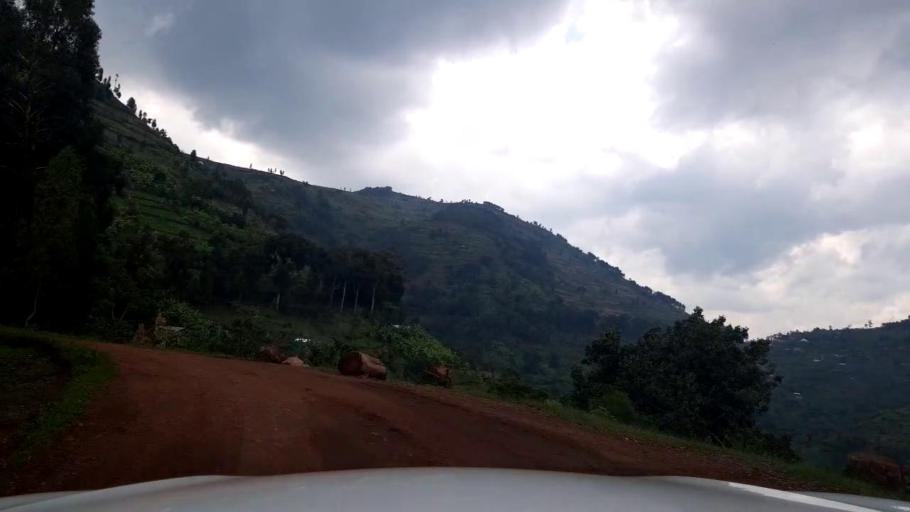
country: UG
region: Western Region
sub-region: Kisoro District
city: Kisoro
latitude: -1.3923
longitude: 29.7974
